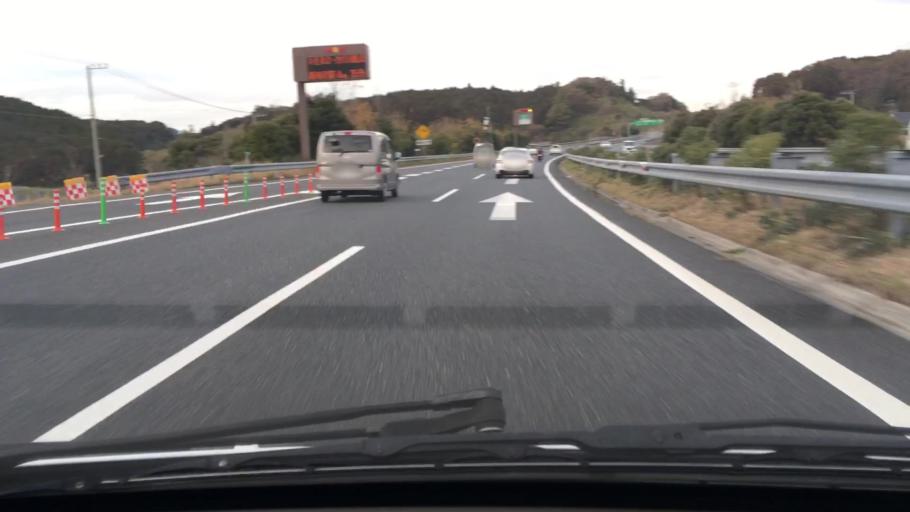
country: JP
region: Chiba
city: Kisarazu
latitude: 35.3476
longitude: 139.9447
